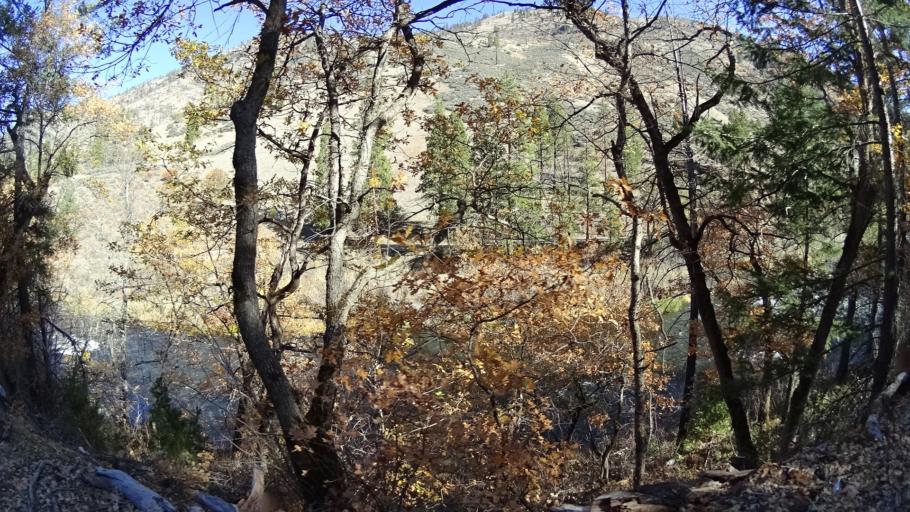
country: US
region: California
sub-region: Siskiyou County
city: Yreka
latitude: 41.8606
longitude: -122.7819
